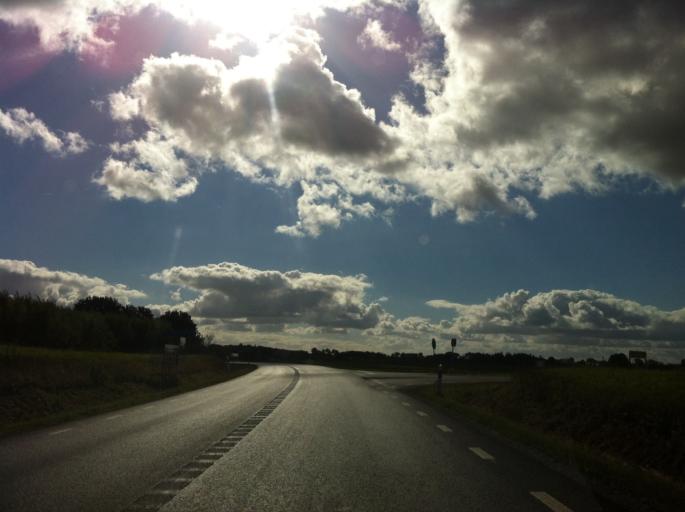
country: SE
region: Skane
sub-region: Tomelilla Kommun
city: Tomelilla
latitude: 55.6437
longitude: 14.0079
